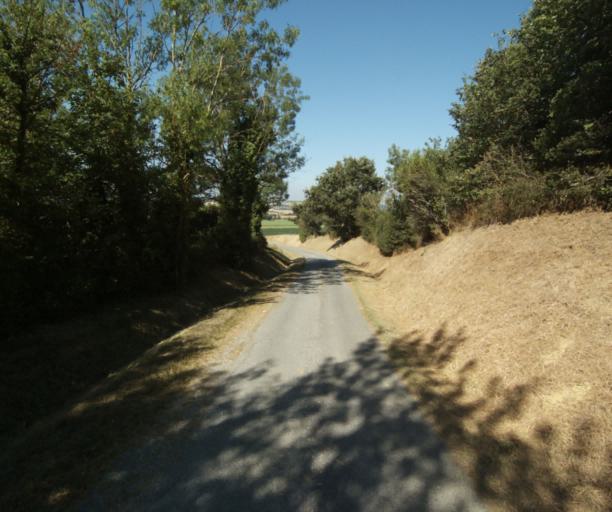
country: FR
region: Midi-Pyrenees
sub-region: Departement de la Haute-Garonne
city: Saint-Felix-Lauragais
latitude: 43.5119
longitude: 1.9315
